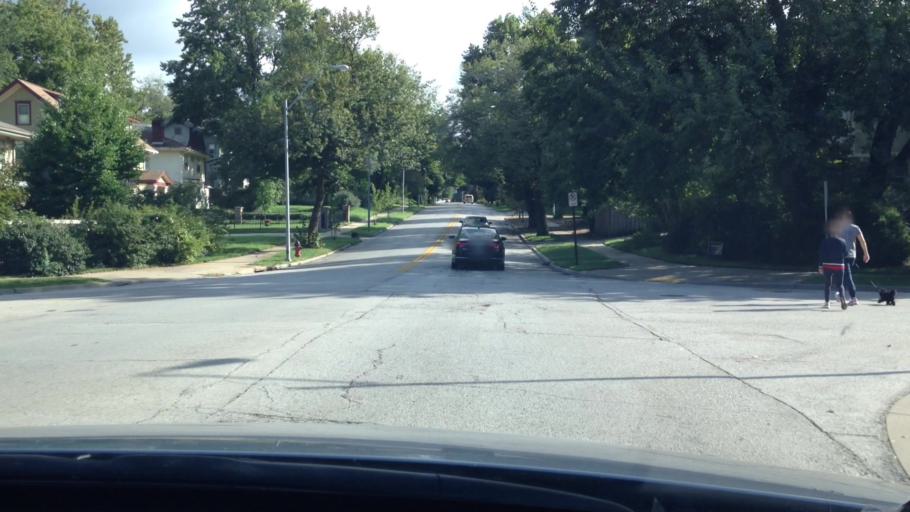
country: US
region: Kansas
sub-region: Johnson County
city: Mission Hills
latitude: 39.0191
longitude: -94.5929
